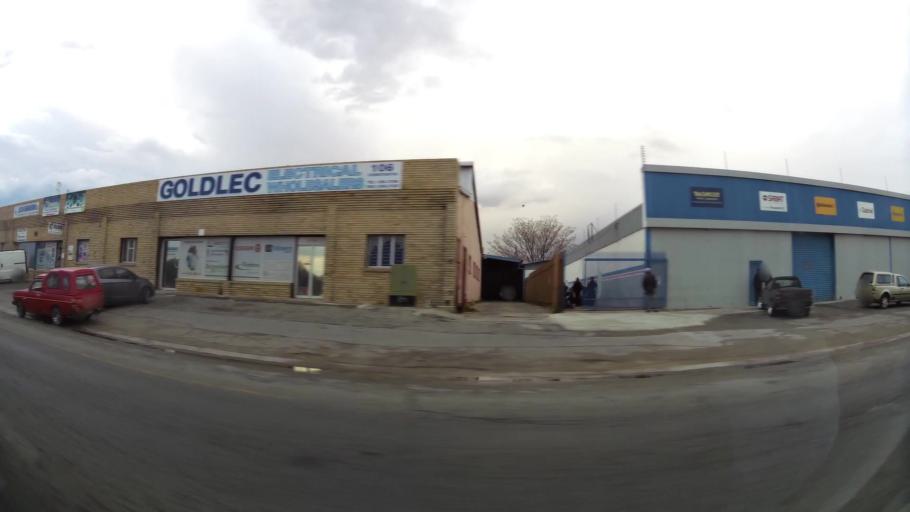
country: ZA
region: Orange Free State
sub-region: Lejweleputswa District Municipality
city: Welkom
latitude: -27.9727
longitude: 26.7572
